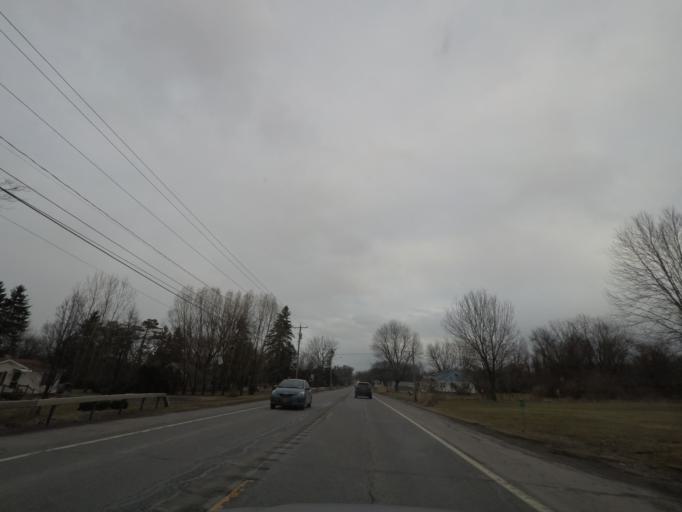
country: US
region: New York
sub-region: Madison County
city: Wampsville
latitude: 43.0744
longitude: -75.7178
